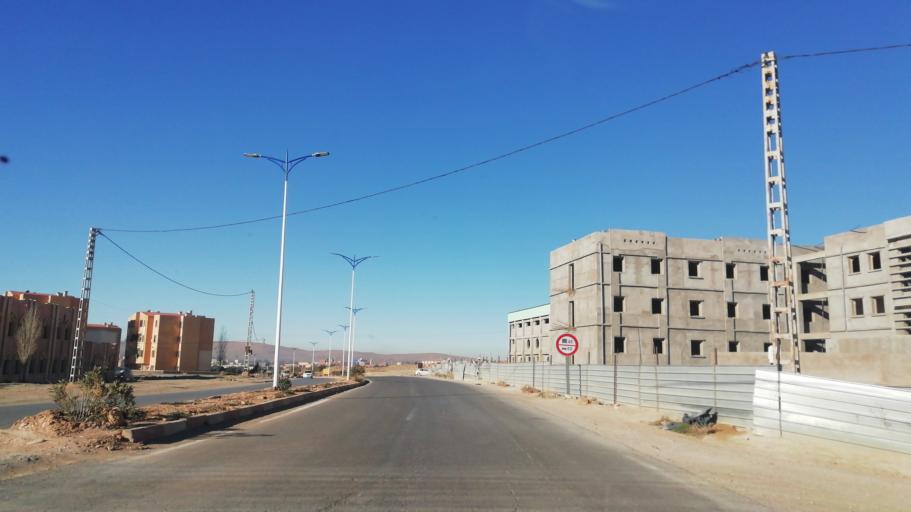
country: DZ
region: El Bayadh
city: El Bayadh
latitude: 33.6878
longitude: 1.0417
